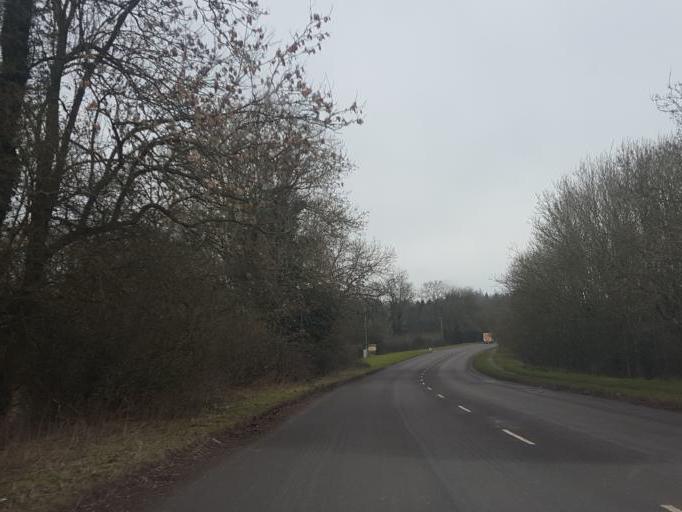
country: GB
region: England
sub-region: Buckinghamshire
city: Stokenchurch
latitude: 51.6631
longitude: -0.9183
